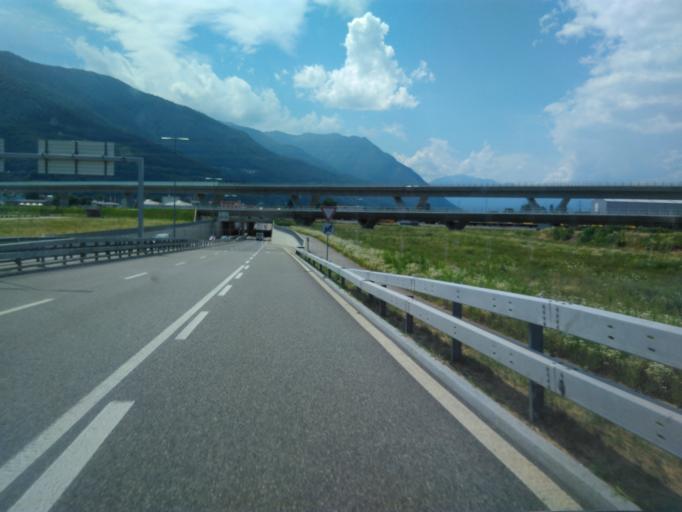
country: CH
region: Ticino
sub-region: Bellinzona District
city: Camorino
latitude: 46.1621
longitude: 8.9880
